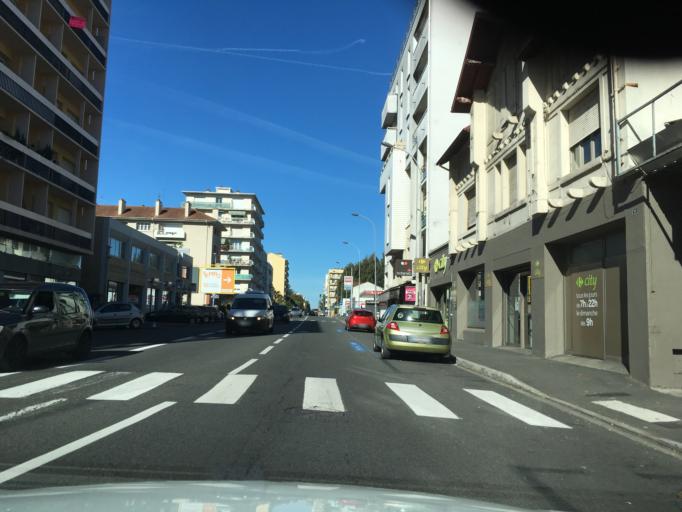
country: FR
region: Aquitaine
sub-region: Departement des Pyrenees-Atlantiques
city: Pau
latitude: 43.3063
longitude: -0.3762
